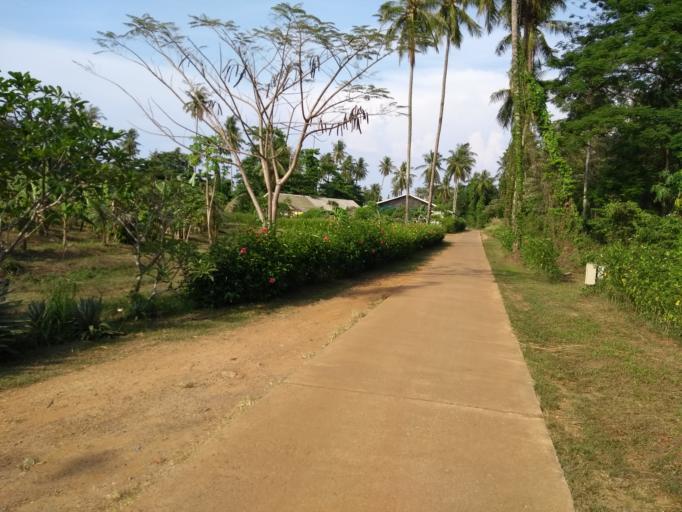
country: TH
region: Trat
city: Ko Kut
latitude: 11.8204
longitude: 102.4672
